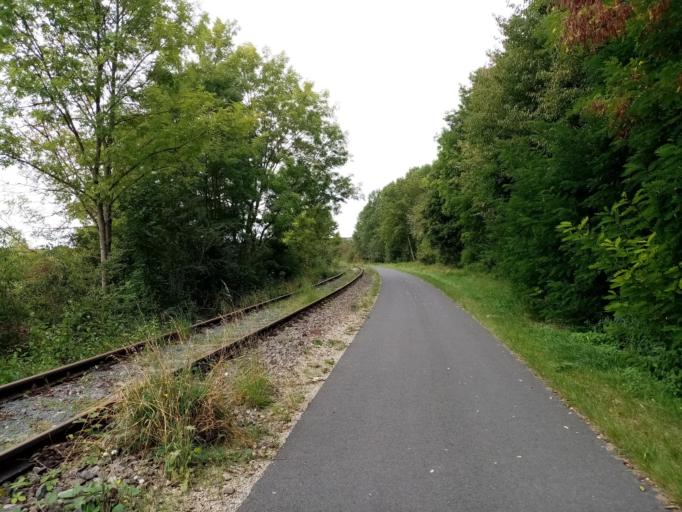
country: DE
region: Thuringia
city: Dingelstadt
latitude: 51.3261
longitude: 10.3132
